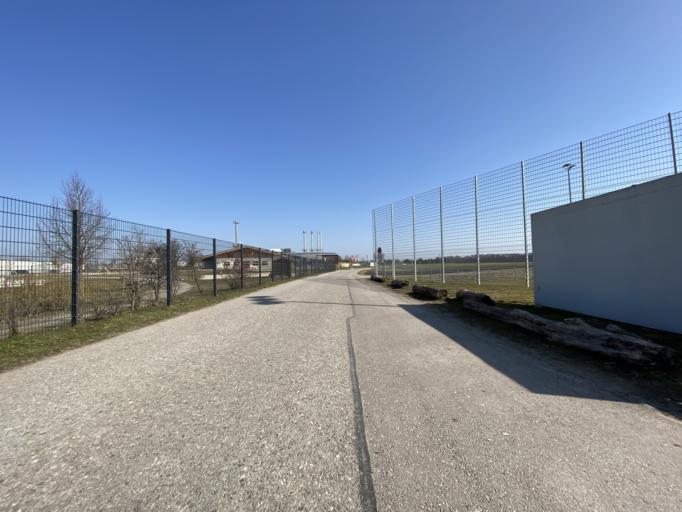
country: DE
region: Bavaria
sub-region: Upper Bavaria
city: Unterfoehring
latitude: 48.1917
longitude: 11.6586
